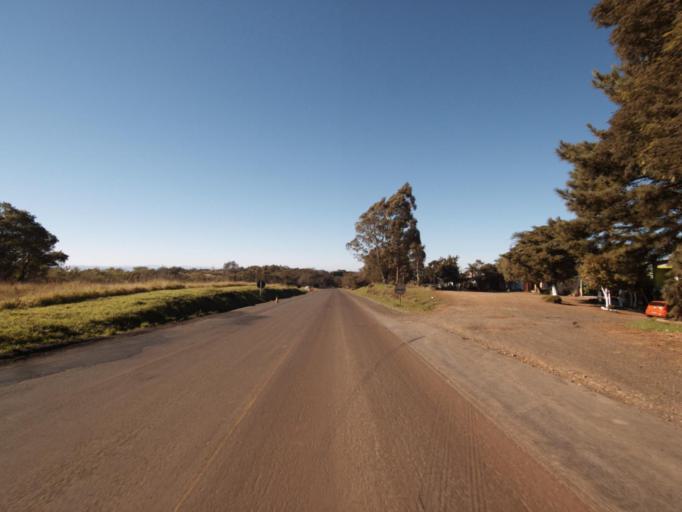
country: AR
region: Misiones
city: Bernardo de Irigoyen
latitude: -26.7639
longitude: -53.4968
